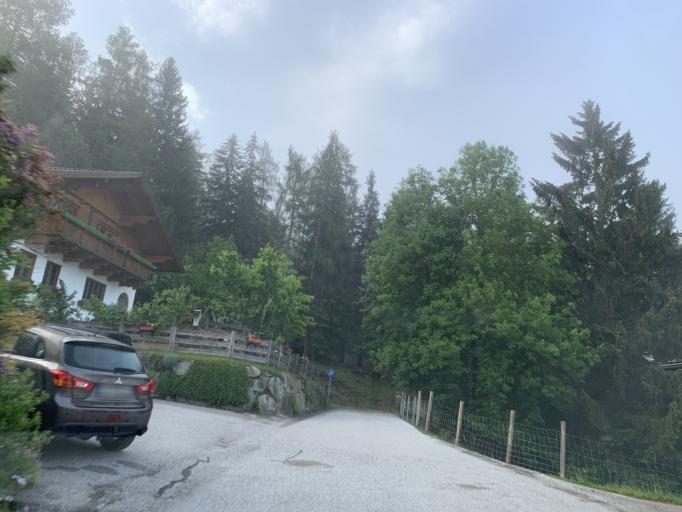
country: AT
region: Salzburg
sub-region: Politischer Bezirk Sankt Johann im Pongau
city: Forstau
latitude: 47.3961
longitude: 13.5941
